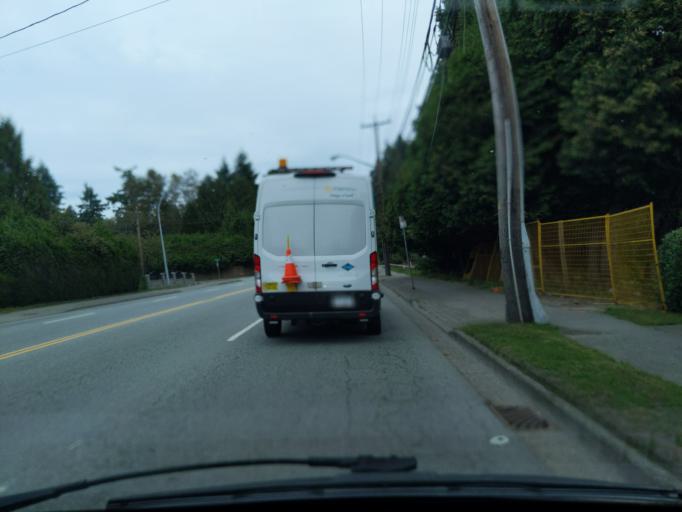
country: CA
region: British Columbia
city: New Westminster
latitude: 49.1988
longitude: -122.8268
